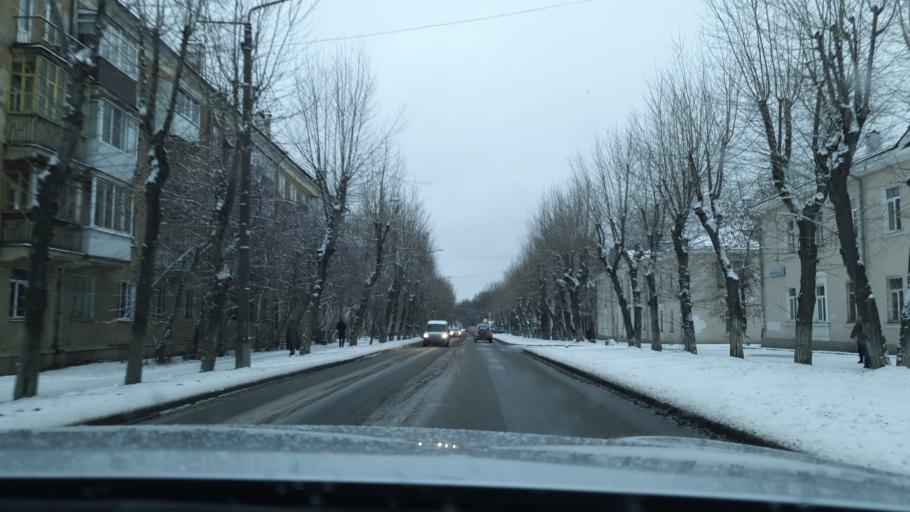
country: RU
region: Sverdlovsk
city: Istok
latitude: 56.7549
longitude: 60.7083
